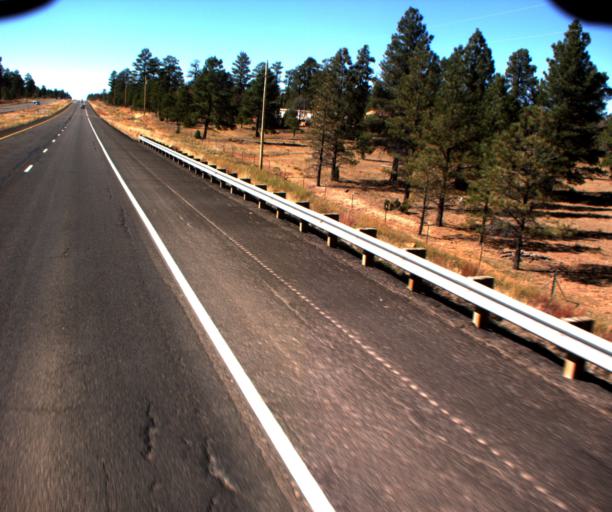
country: US
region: Arizona
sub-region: Apache County
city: Saint Michaels
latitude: 35.6741
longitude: -109.1809
